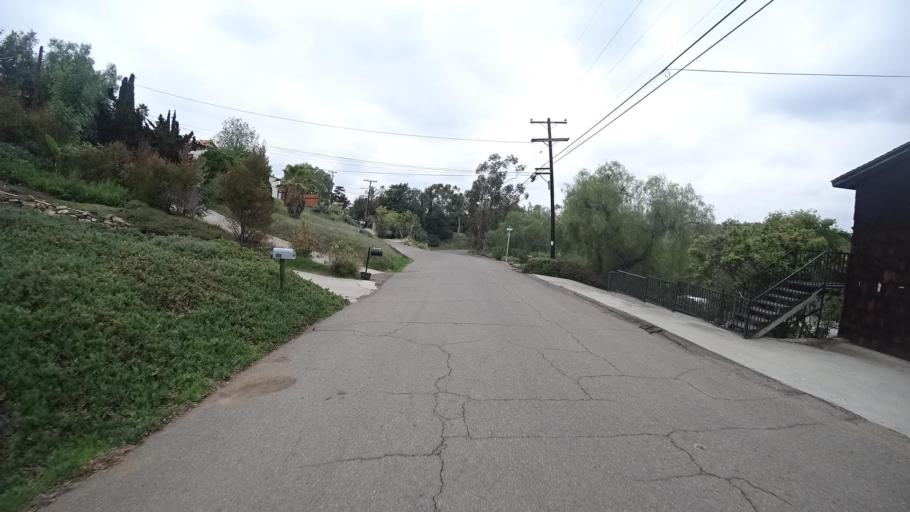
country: US
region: California
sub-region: San Diego County
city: Spring Valley
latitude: 32.7375
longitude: -116.9969
